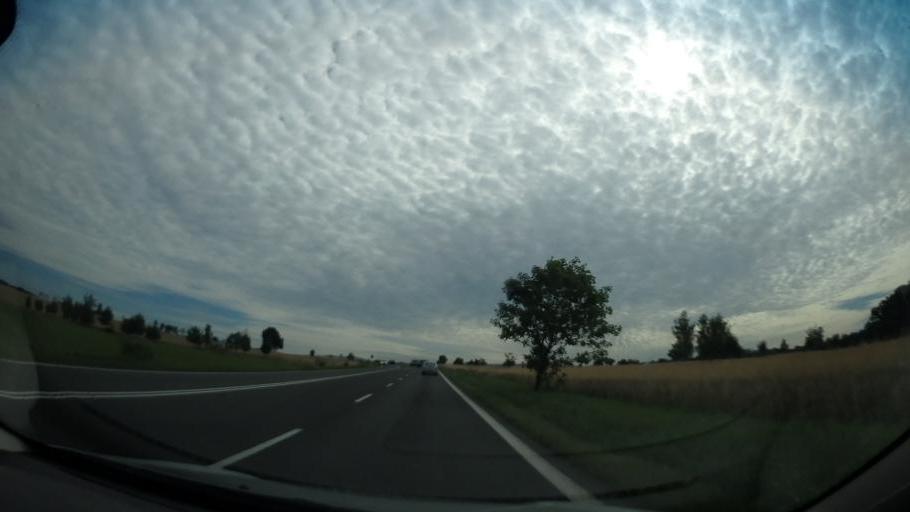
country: CZ
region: Olomoucky
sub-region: Okres Sumperk
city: Bludov
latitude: 49.9413
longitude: 16.9388
